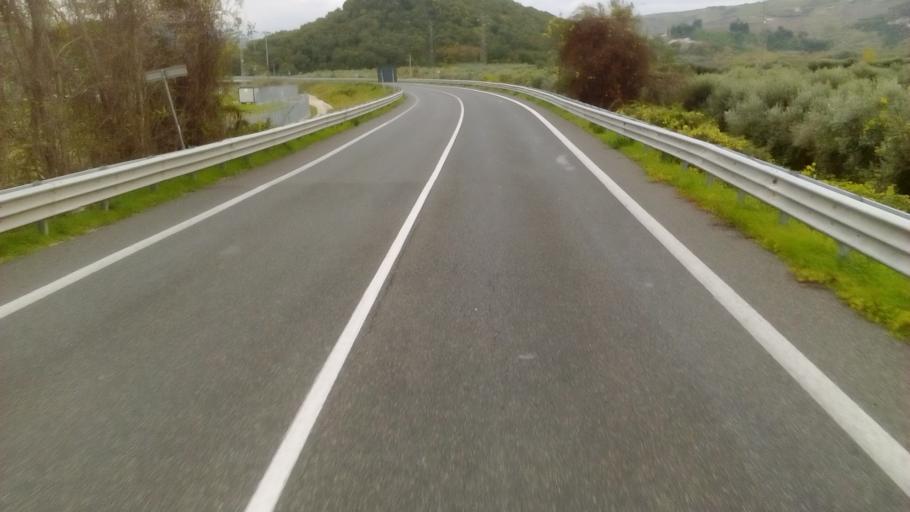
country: IT
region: Abruzzo
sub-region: Provincia di Chieti
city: San Salvo
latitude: 42.0056
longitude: 14.7212
